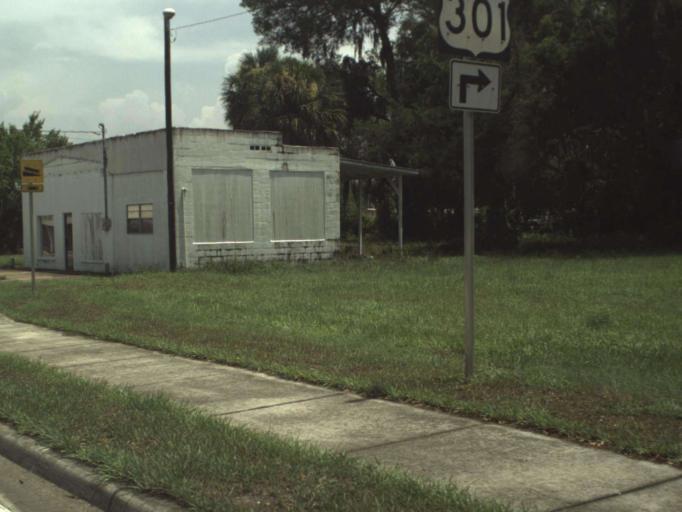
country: US
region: Florida
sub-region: Sumter County
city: Lake Panasoffkee
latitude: 28.7989
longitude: -82.0705
